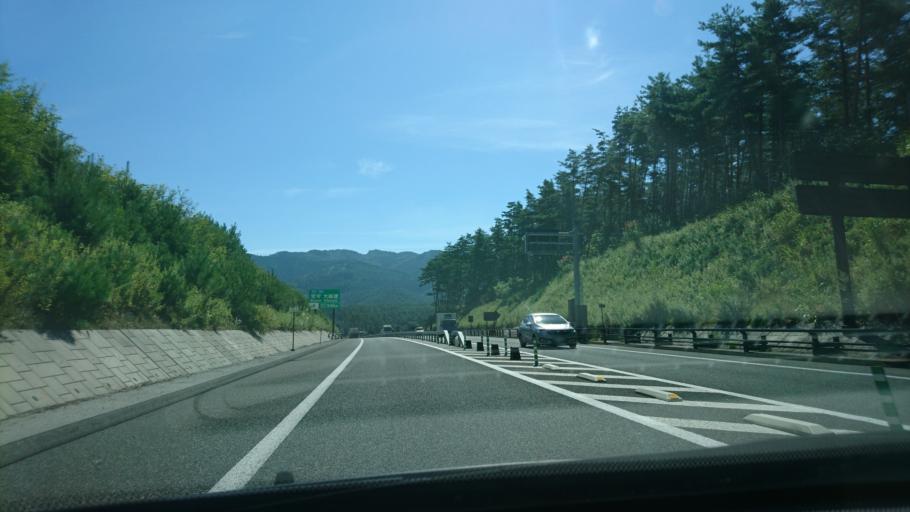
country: JP
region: Iwate
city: Tono
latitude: 39.2940
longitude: 141.3932
